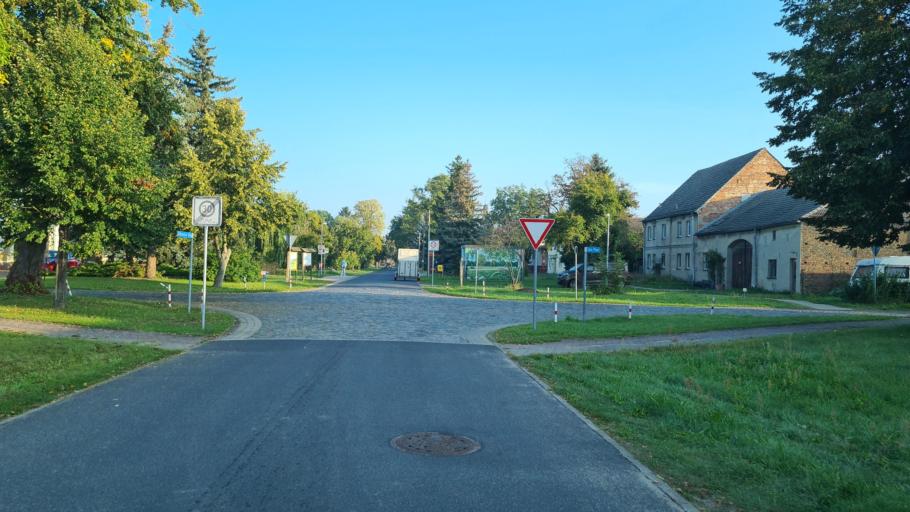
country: DE
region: Brandenburg
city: Luckenwalde
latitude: 52.0985
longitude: 13.0732
